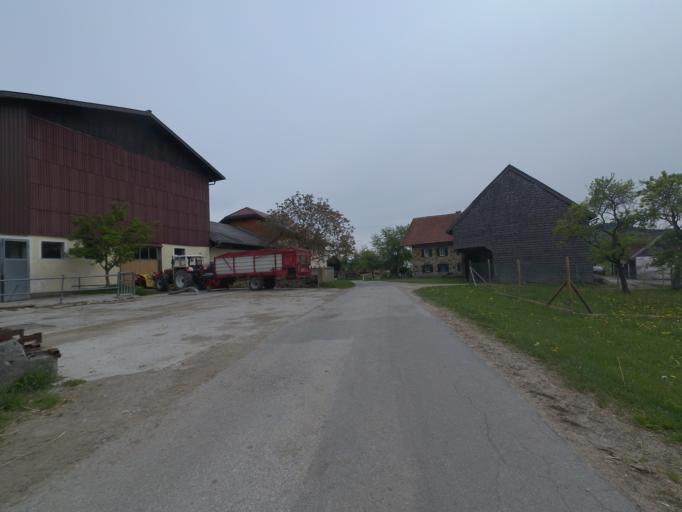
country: AT
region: Salzburg
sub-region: Politischer Bezirk Salzburg-Umgebung
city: Mattsee
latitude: 47.9737
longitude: 13.1276
